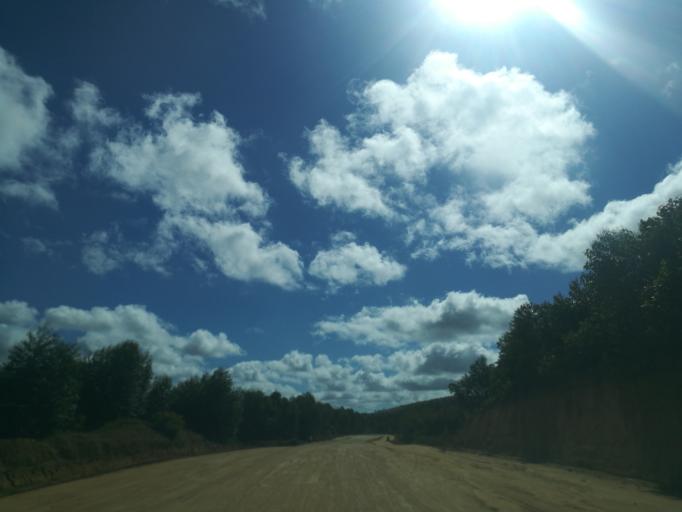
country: MG
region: Alaotra Mangoro
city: Moramanga
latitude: -18.7110
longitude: 48.2705
